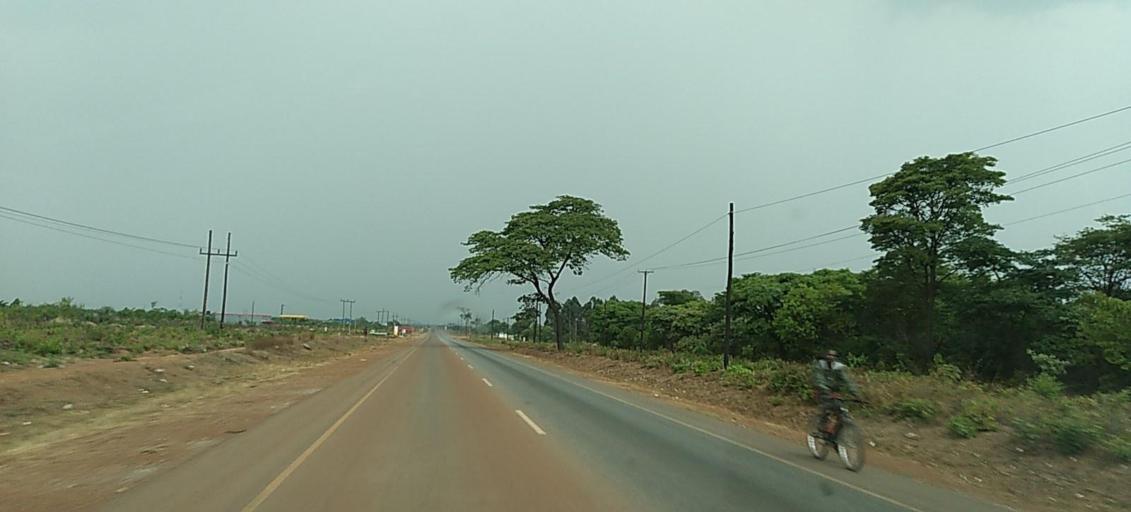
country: ZM
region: Copperbelt
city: Kalulushi
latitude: -12.8343
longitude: 28.1153
